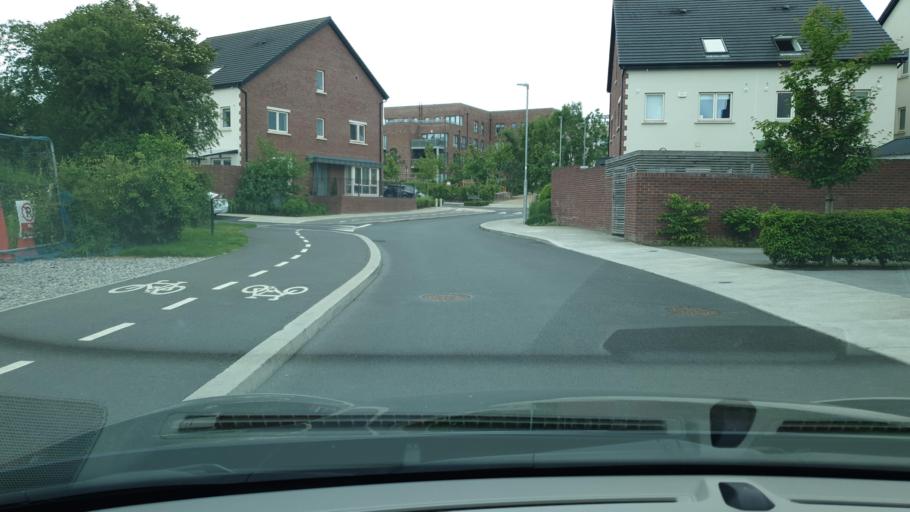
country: IE
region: Leinster
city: Lucan
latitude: 53.3478
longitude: -6.4705
